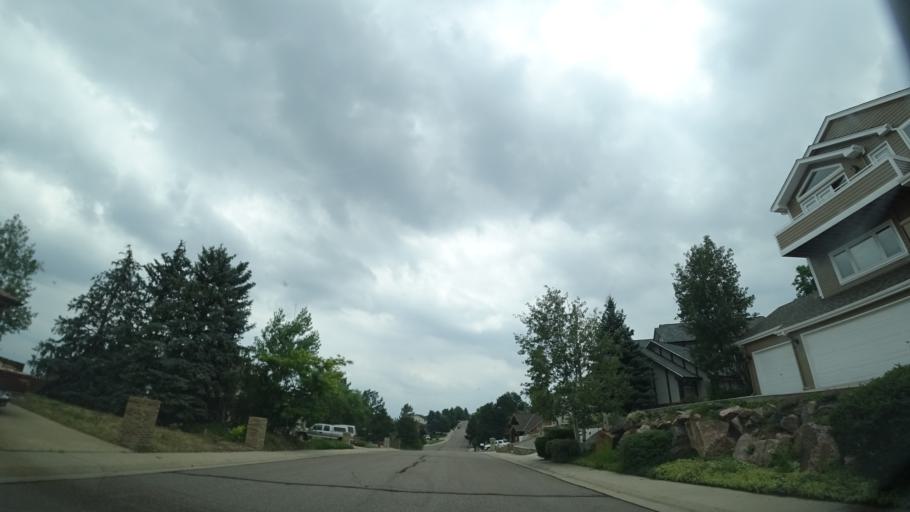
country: US
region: Colorado
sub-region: Jefferson County
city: West Pleasant View
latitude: 39.7071
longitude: -105.1613
